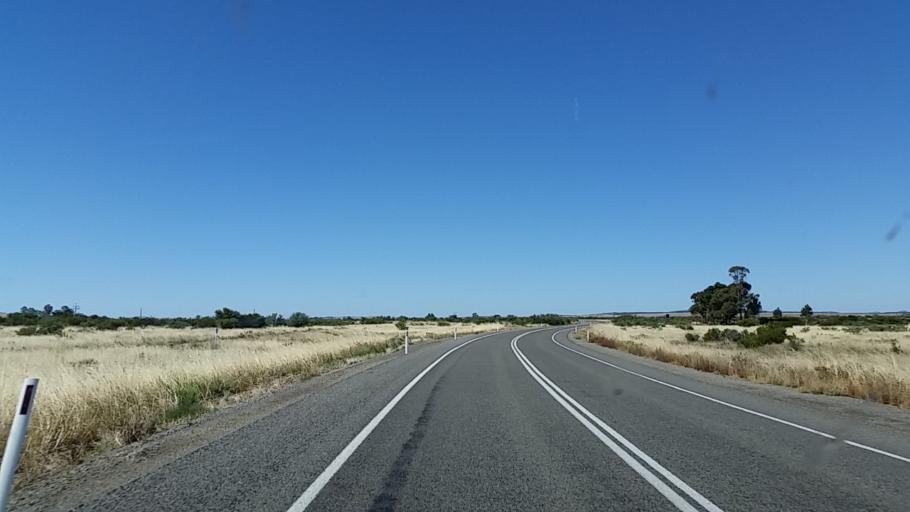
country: AU
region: South Australia
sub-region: Peterborough
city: Peterborough
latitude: -33.1727
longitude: 138.9100
